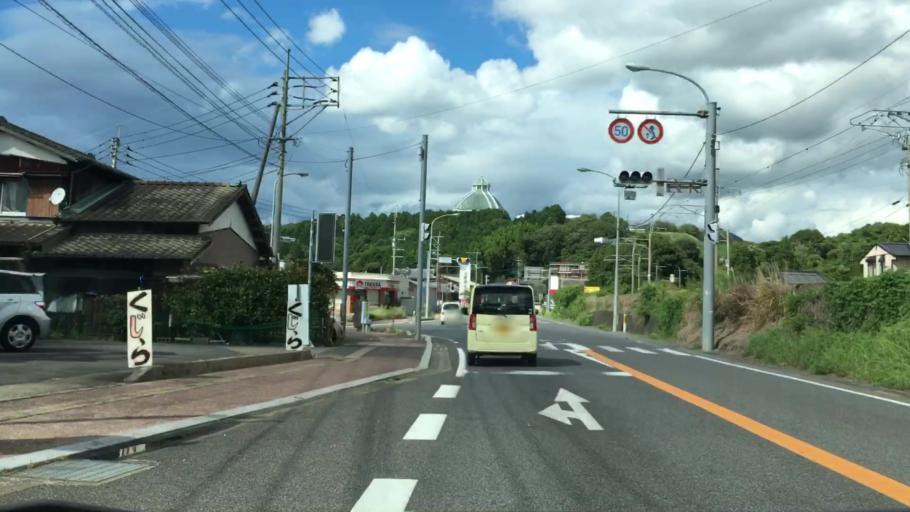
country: JP
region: Saga Prefecture
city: Imaricho-ko
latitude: 33.1845
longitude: 129.8543
